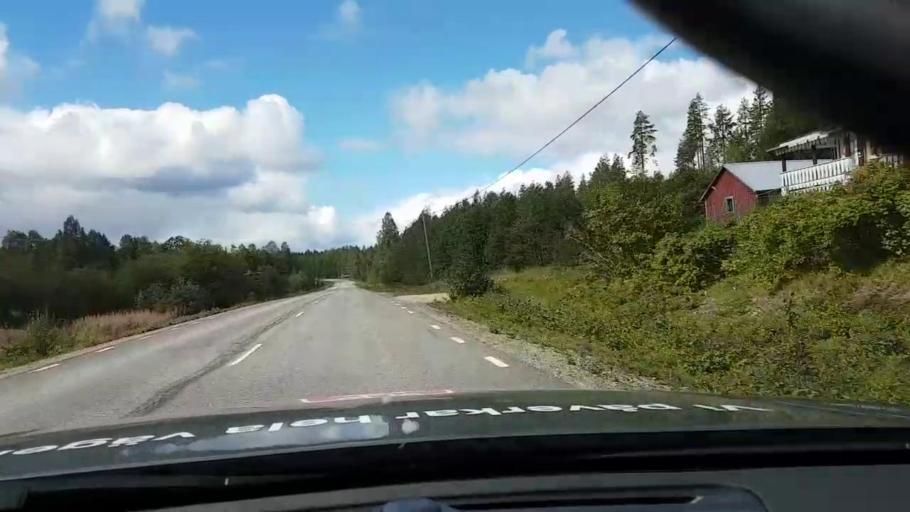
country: SE
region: Vaesternorrland
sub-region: OErnskoeldsviks Kommun
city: Bredbyn
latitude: 63.5285
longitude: 17.9910
